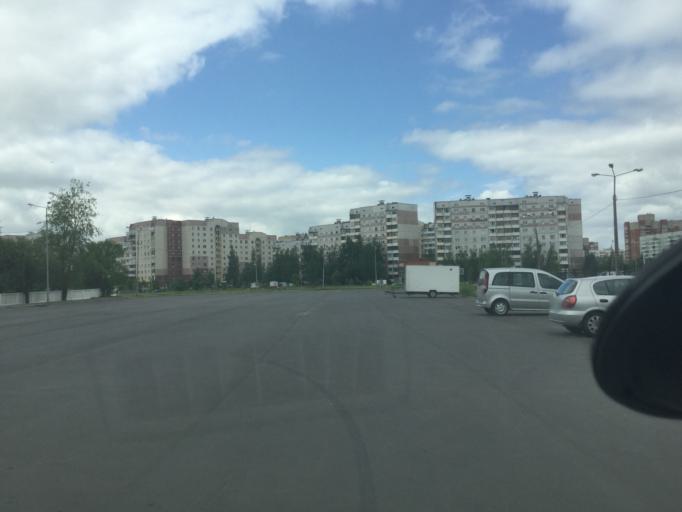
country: BY
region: Vitebsk
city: Vitebsk
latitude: 55.1601
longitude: 30.2238
